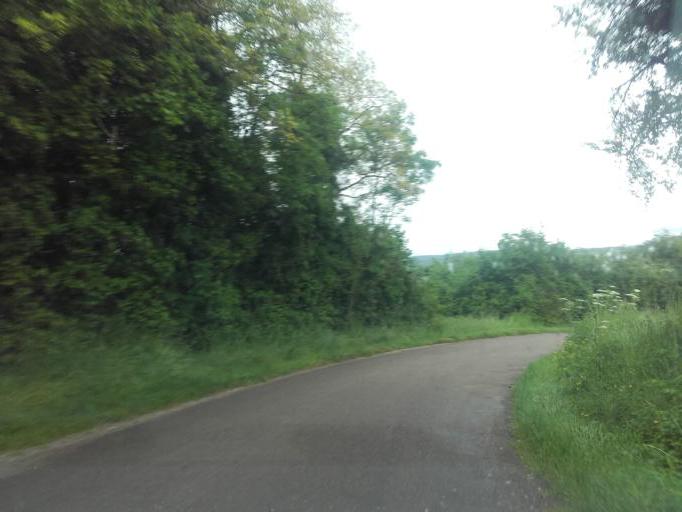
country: FR
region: Bourgogne
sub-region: Departement de la Cote-d'Or
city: Nolay
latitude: 46.9896
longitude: 4.6814
